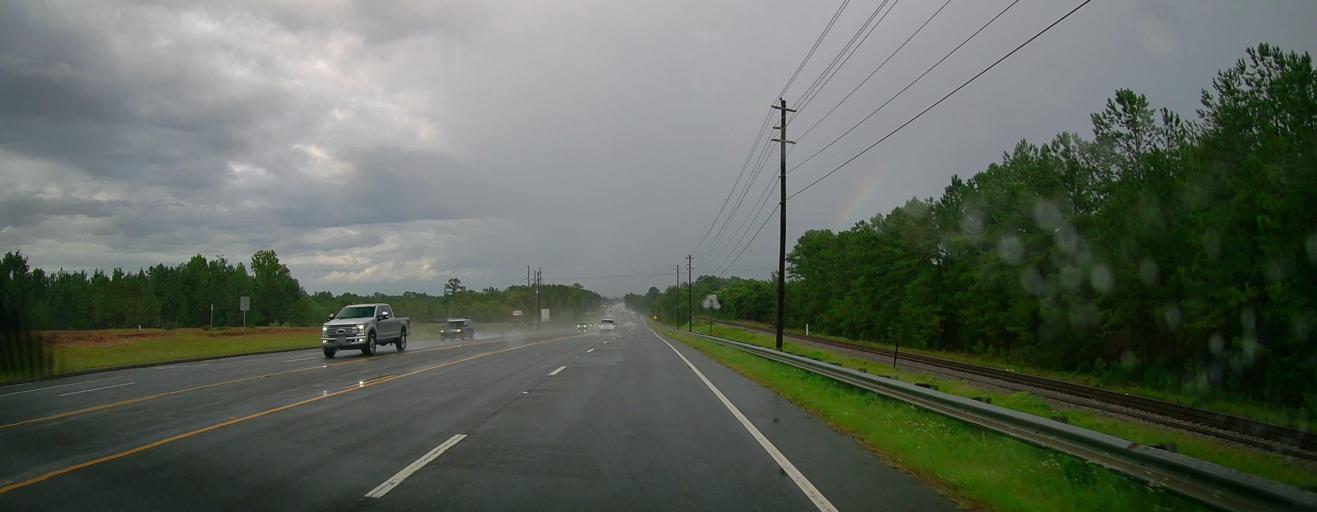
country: US
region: Georgia
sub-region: Ware County
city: Sunnyside
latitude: 31.2326
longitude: -82.3299
